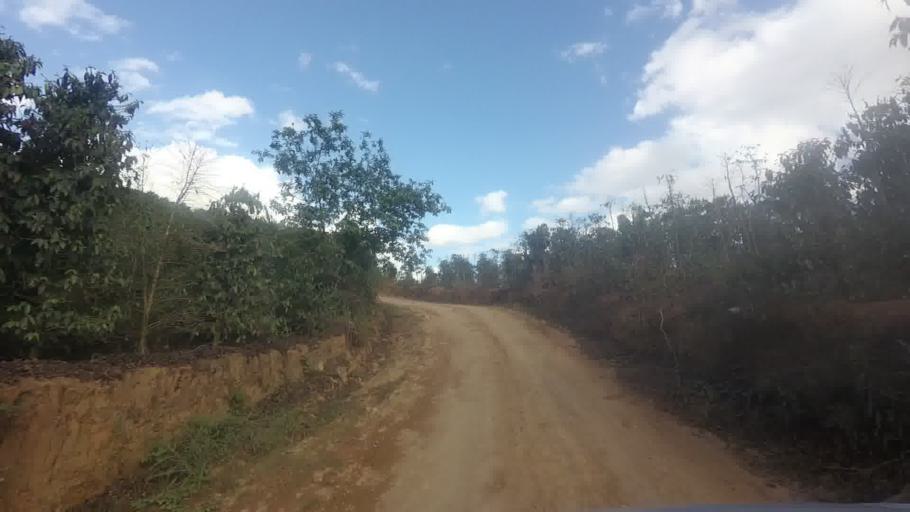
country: BR
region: Espirito Santo
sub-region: Sao Jose Do Calcado
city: Sao Jose do Calcado
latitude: -20.9856
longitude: -41.5196
